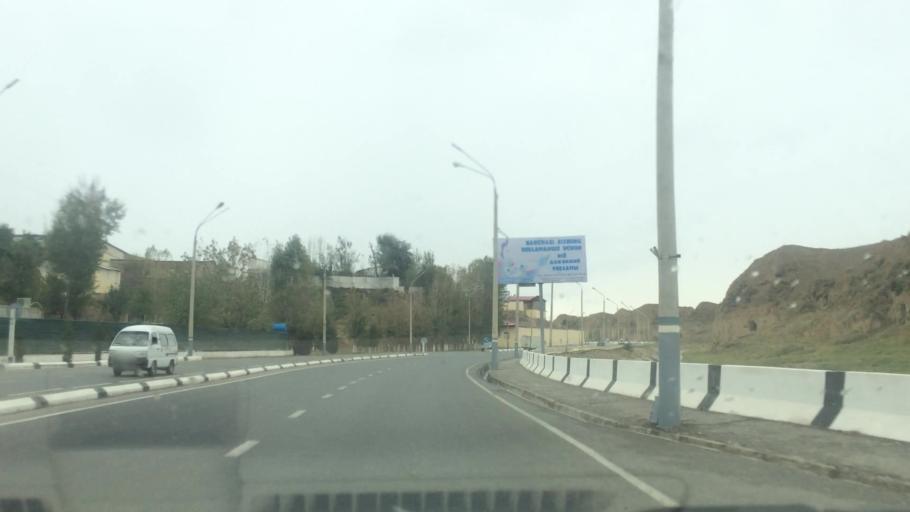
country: UZ
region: Samarqand
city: Samarqand
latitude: 39.6695
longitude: 66.9987
